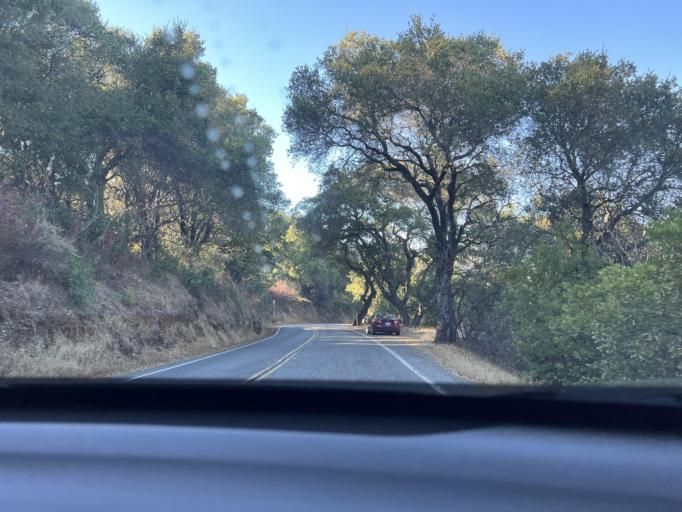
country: US
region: California
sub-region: Santa Clara County
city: Loyola
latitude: 37.2874
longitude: -122.0883
